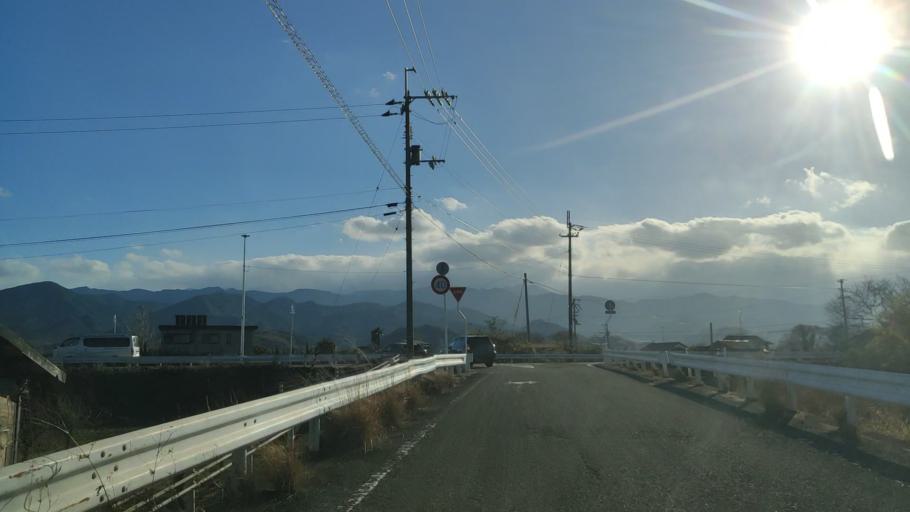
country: JP
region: Ehime
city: Saijo
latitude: 33.9088
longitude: 133.0970
